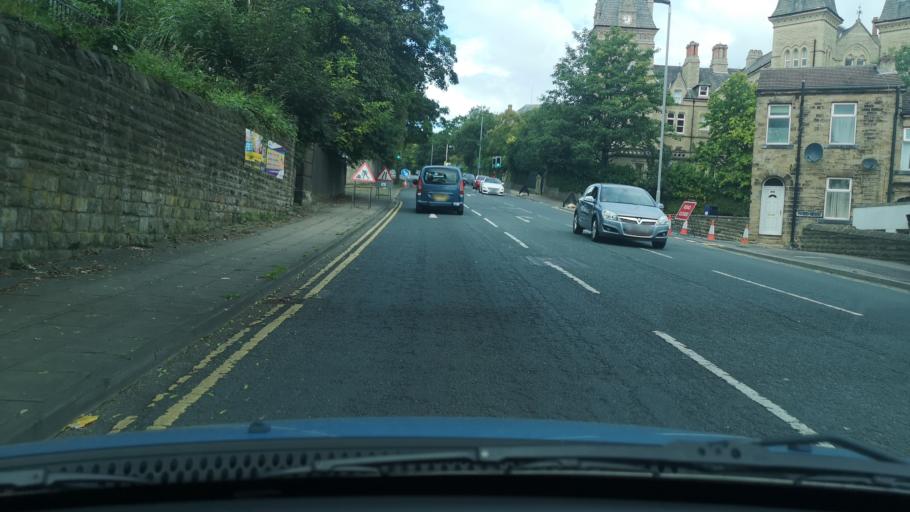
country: GB
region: England
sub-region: Kirklees
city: Dewsbury
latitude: 53.6954
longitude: -1.6349
